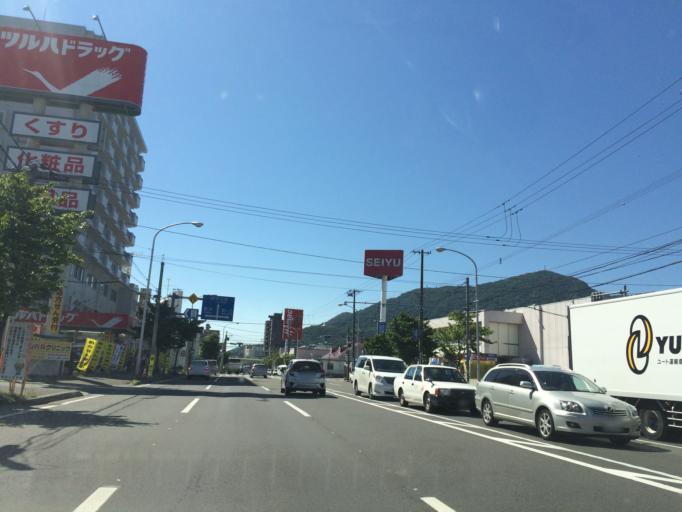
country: JP
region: Hokkaido
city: Sapporo
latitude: 43.0469
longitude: 141.3227
